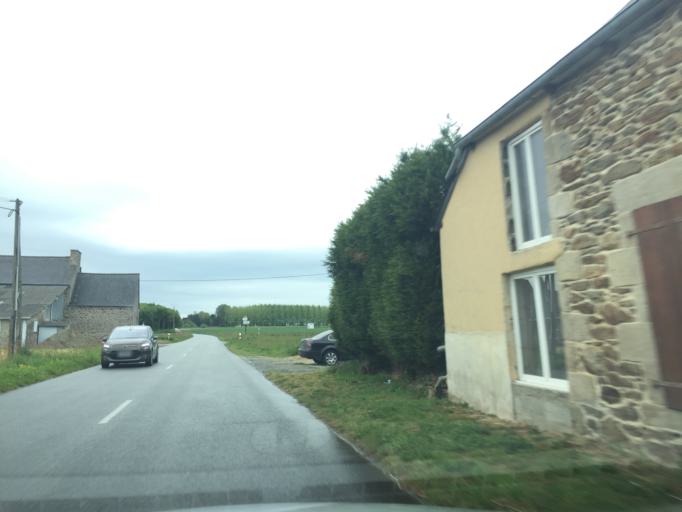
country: FR
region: Brittany
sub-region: Departement des Cotes-d'Armor
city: Crehen
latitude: 48.5595
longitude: -2.2406
